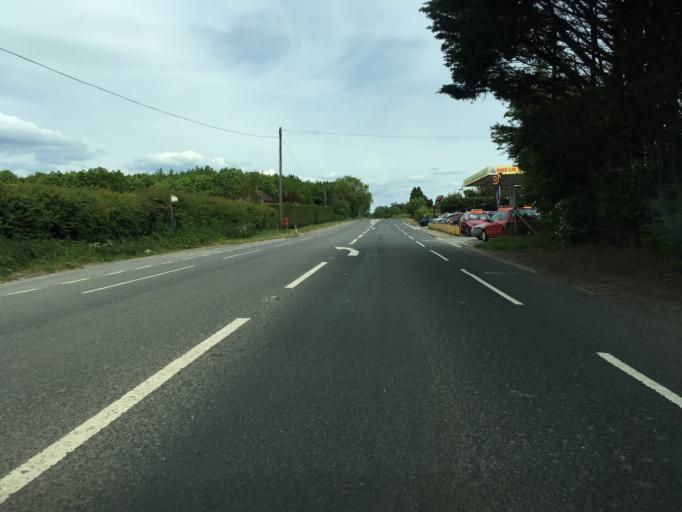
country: GB
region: England
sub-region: Gloucestershire
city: Stonehouse
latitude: 51.7937
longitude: -2.3069
